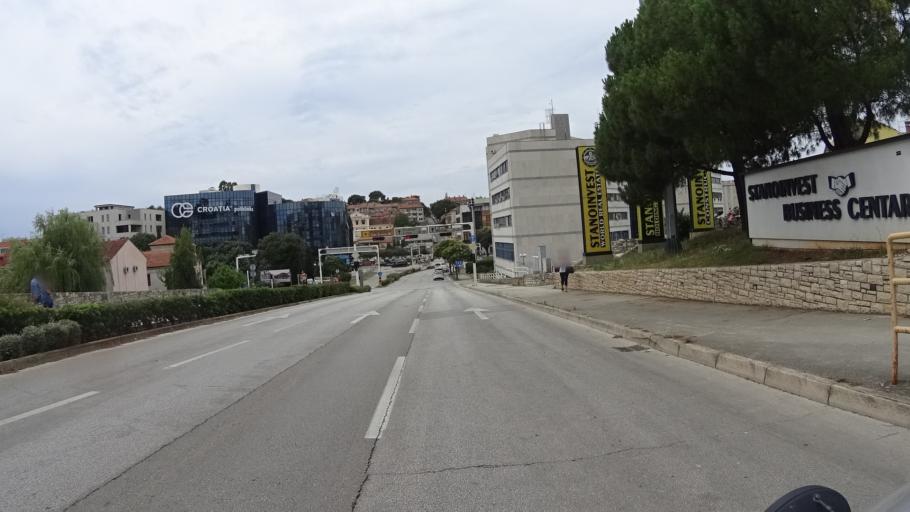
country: HR
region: Istarska
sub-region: Grad Pula
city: Pula
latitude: 44.8647
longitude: 13.8519
